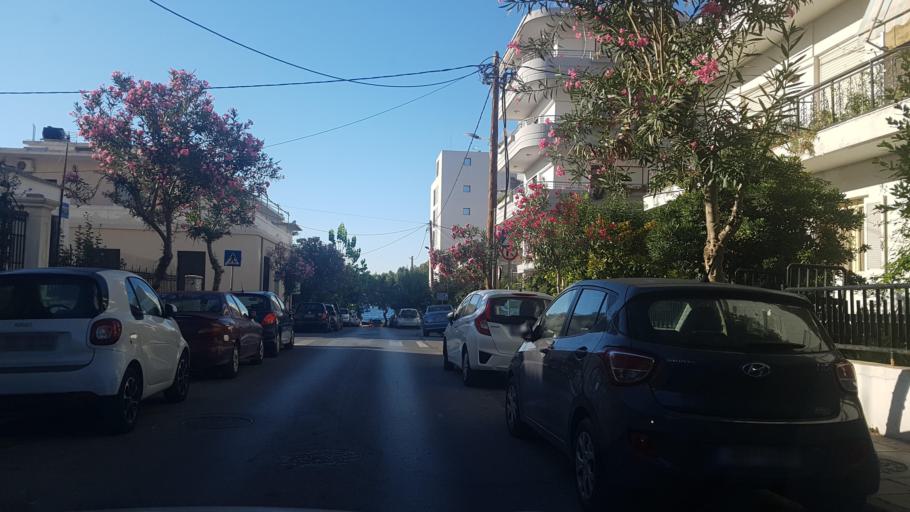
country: GR
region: Crete
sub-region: Nomos Chanias
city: Chania
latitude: 35.5166
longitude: 24.0129
